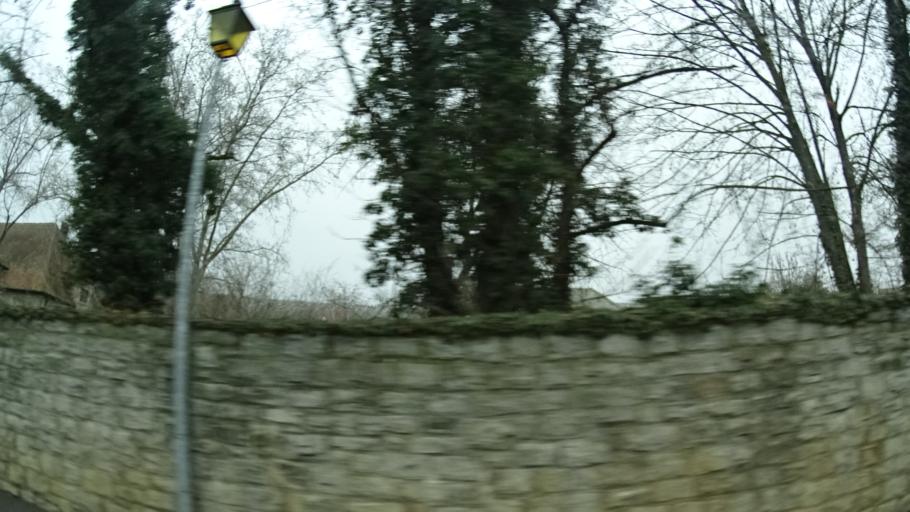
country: DE
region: Bavaria
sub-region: Regierungsbezirk Unterfranken
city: Frickenhausen
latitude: 49.6706
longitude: 10.0898
